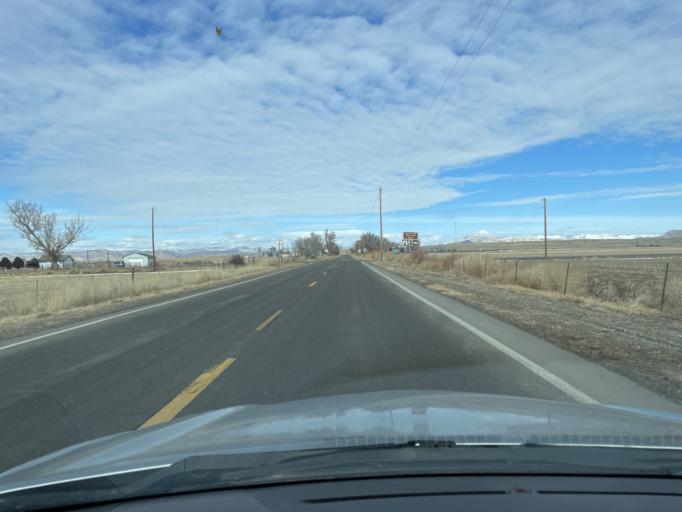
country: US
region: Colorado
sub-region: Mesa County
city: Loma
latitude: 39.2505
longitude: -108.8129
